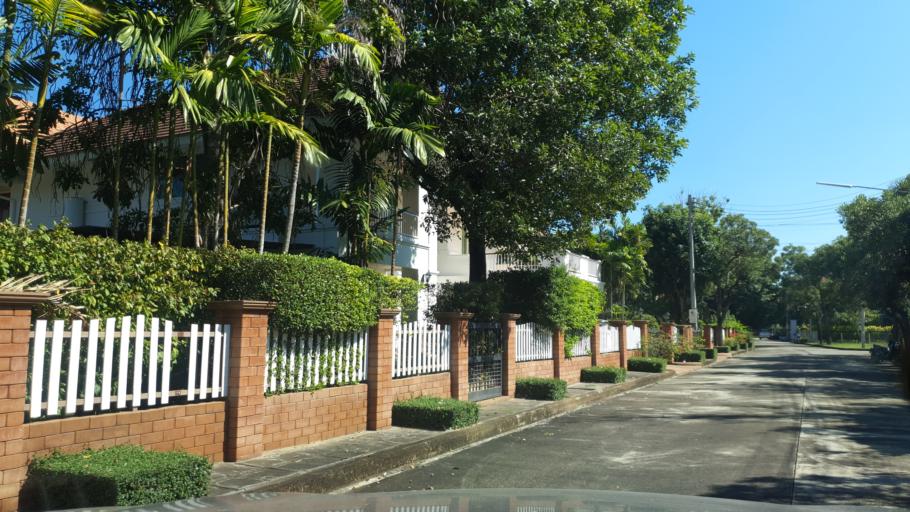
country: TH
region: Chiang Mai
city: Hang Dong
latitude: 18.7339
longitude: 98.9435
